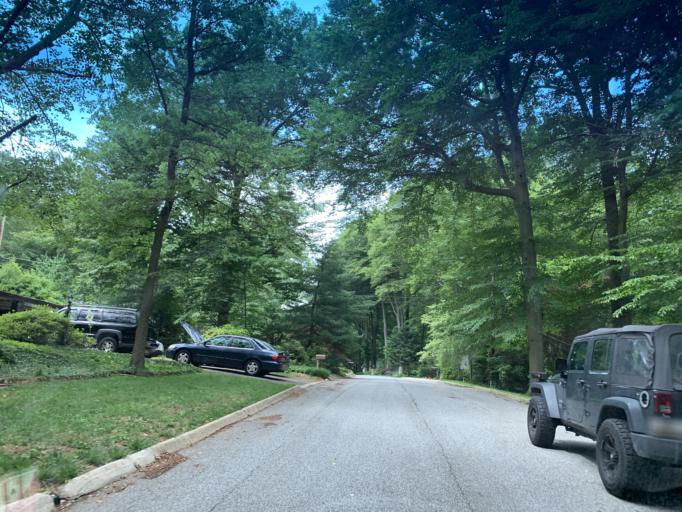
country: US
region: Maryland
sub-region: Harford County
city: Bel Air North
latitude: 39.5325
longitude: -76.3854
